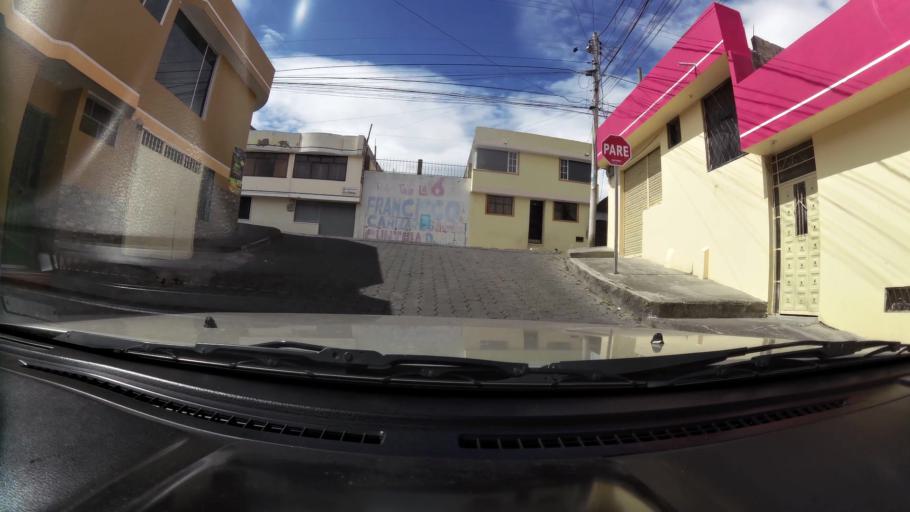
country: EC
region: Cotopaxi
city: Latacunga
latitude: -0.9317
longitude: -78.6002
